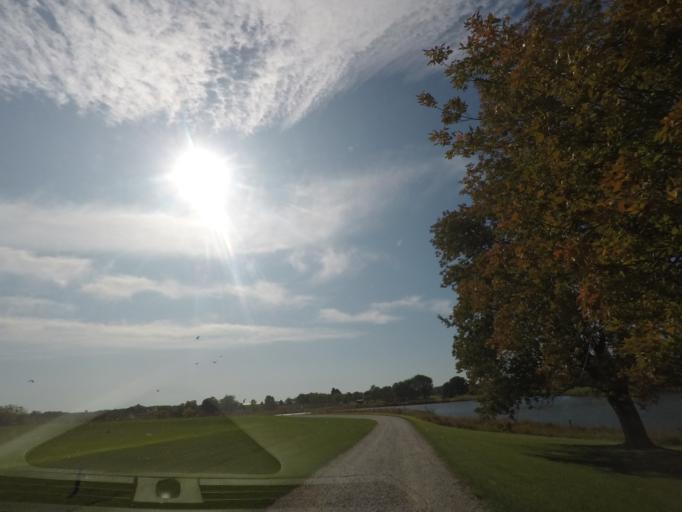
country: US
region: Iowa
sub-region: Story County
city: Gilbert
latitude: 42.1117
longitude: -93.5829
